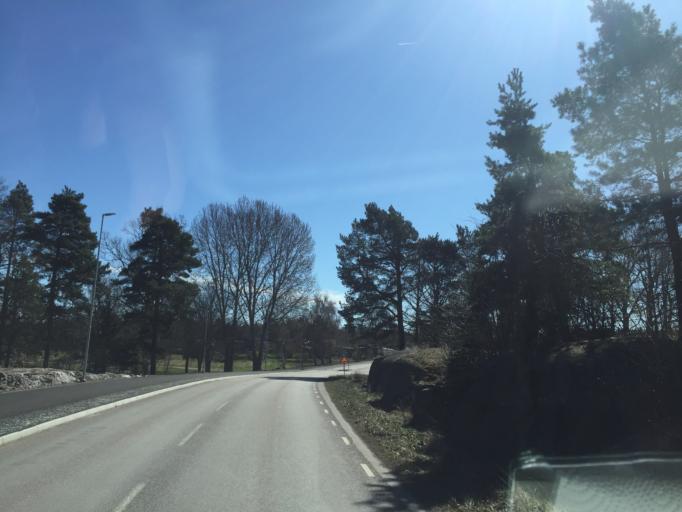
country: SE
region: Kalmar
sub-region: Oskarshamns Kommun
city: Oskarshamn
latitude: 57.2462
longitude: 16.4703
